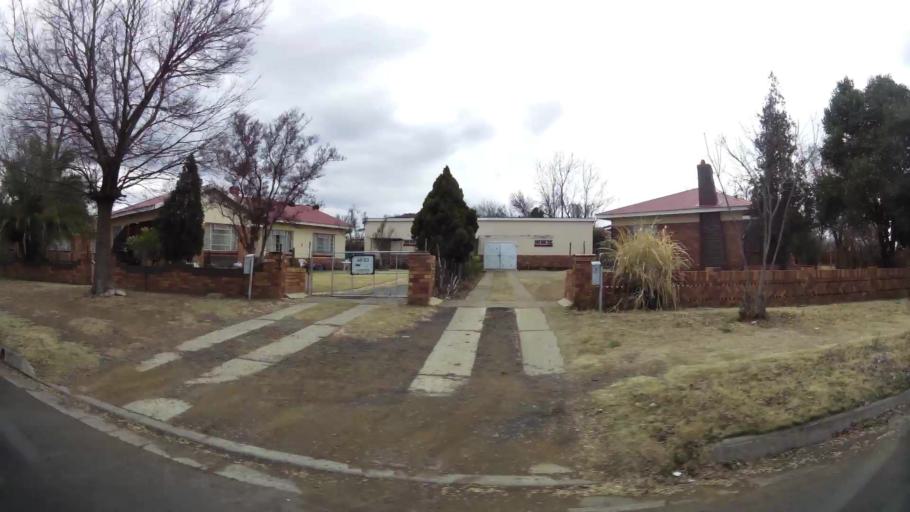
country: ZA
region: Orange Free State
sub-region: Fezile Dabi District Municipality
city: Kroonstad
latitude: -27.6318
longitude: 27.2303
